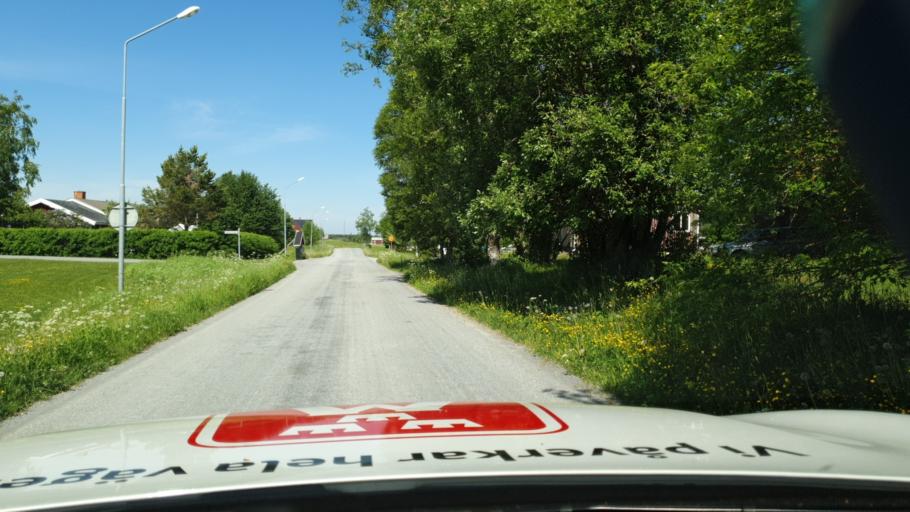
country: SE
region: Jaemtland
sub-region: Bergs Kommun
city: Hoverberg
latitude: 62.9996
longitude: 14.3941
